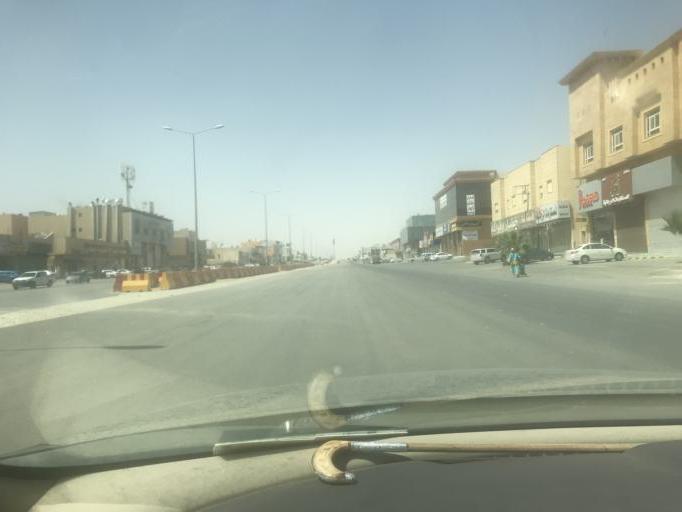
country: SA
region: Ar Riyad
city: Riyadh
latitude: 24.8065
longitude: 46.6026
